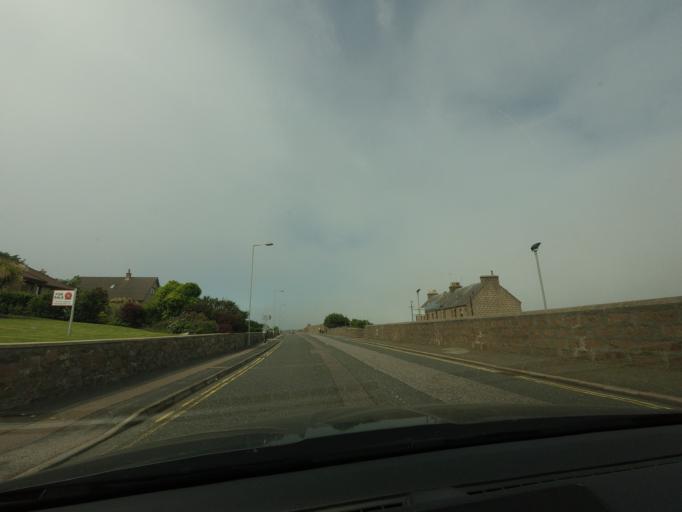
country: GB
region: Scotland
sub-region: Aberdeenshire
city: Peterhead
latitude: 57.4919
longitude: -1.7939
